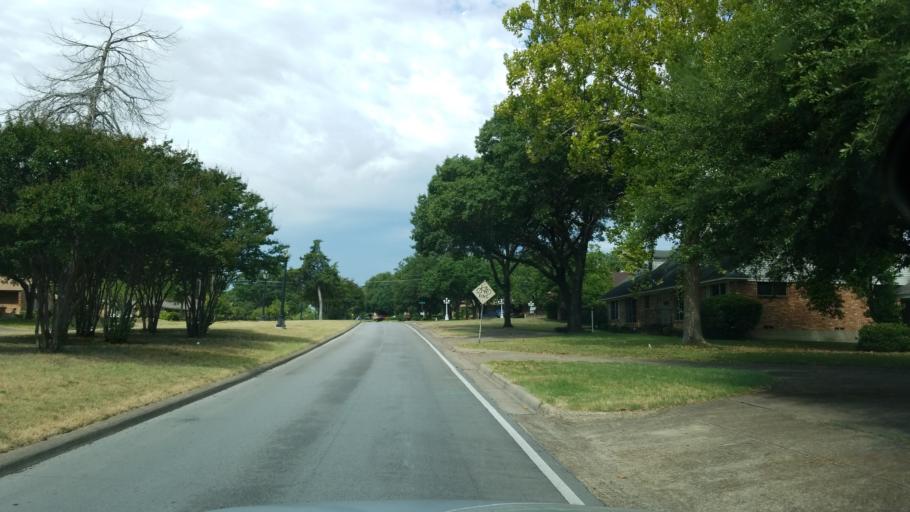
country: US
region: Texas
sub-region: Dallas County
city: Duncanville
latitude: 32.6728
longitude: -96.8438
